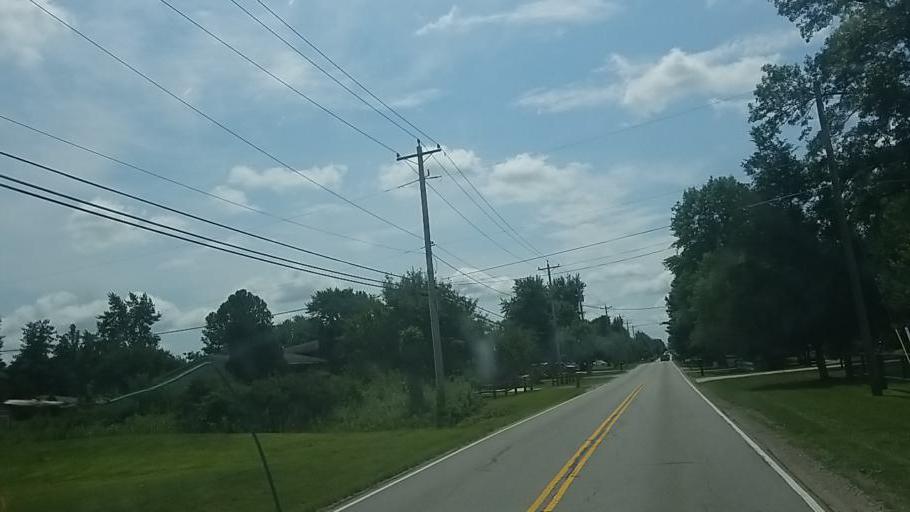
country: US
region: Ohio
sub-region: Franklin County
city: Reynoldsburg
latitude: 39.9949
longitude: -82.7674
